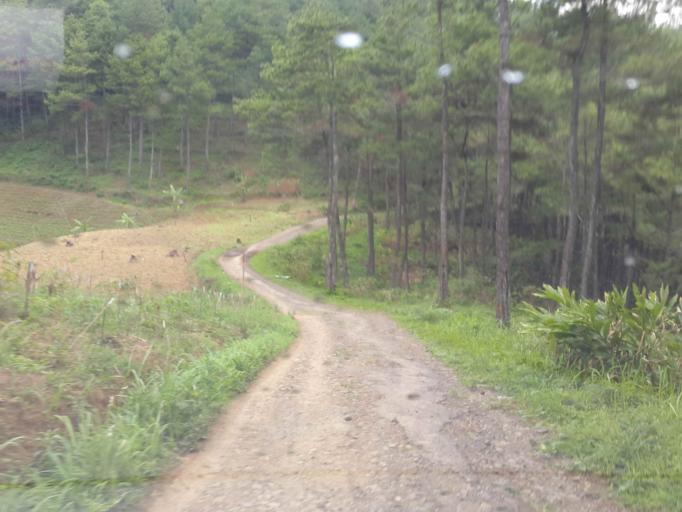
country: ID
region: Central Java
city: Jambuluwuk
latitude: -7.3355
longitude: 108.9557
